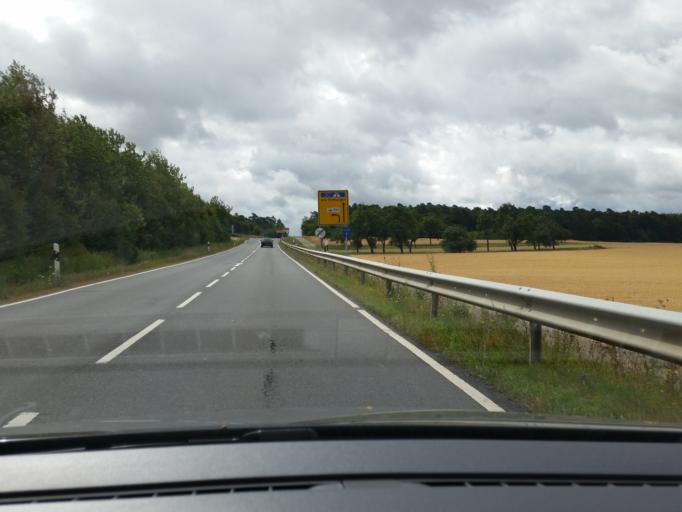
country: DE
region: Baden-Wuerttemberg
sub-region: Karlsruhe Region
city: Osterburken
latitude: 49.4216
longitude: 9.4435
